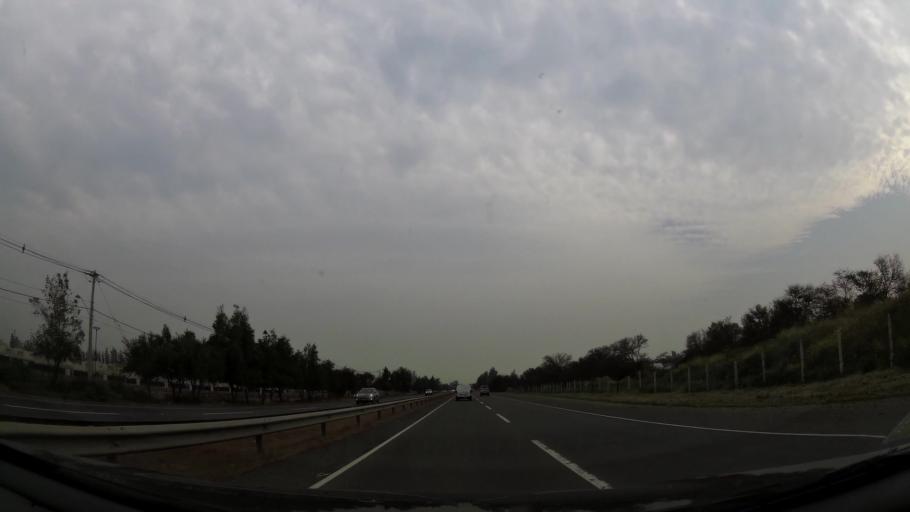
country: CL
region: Santiago Metropolitan
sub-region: Provincia de Chacabuco
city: Chicureo Abajo
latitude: -33.2240
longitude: -70.6815
